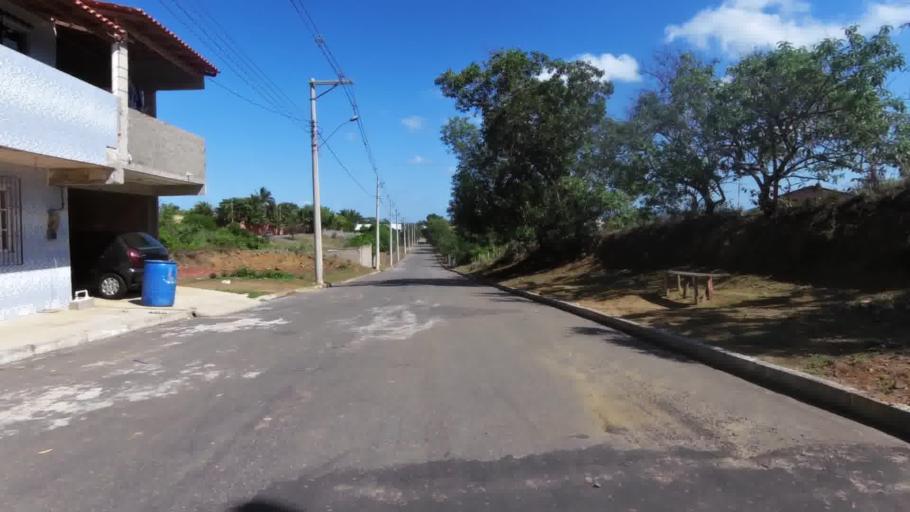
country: BR
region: Espirito Santo
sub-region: Piuma
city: Piuma
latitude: -20.8032
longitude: -40.5981
